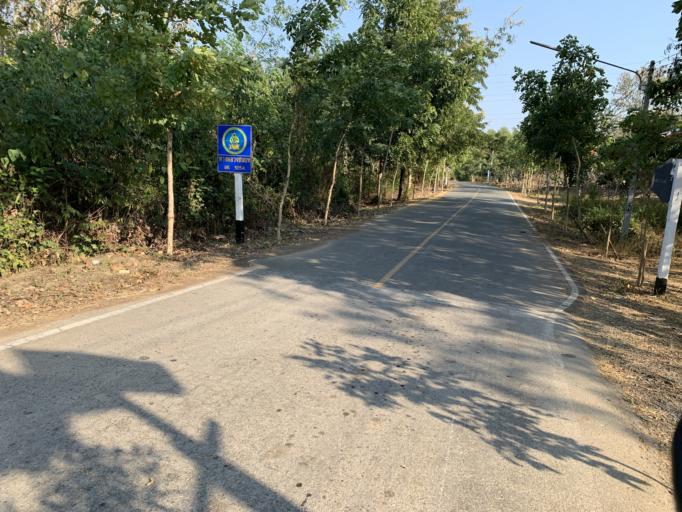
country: TH
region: Uttaradit
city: Tha Pla
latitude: 17.6950
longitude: 100.4092
